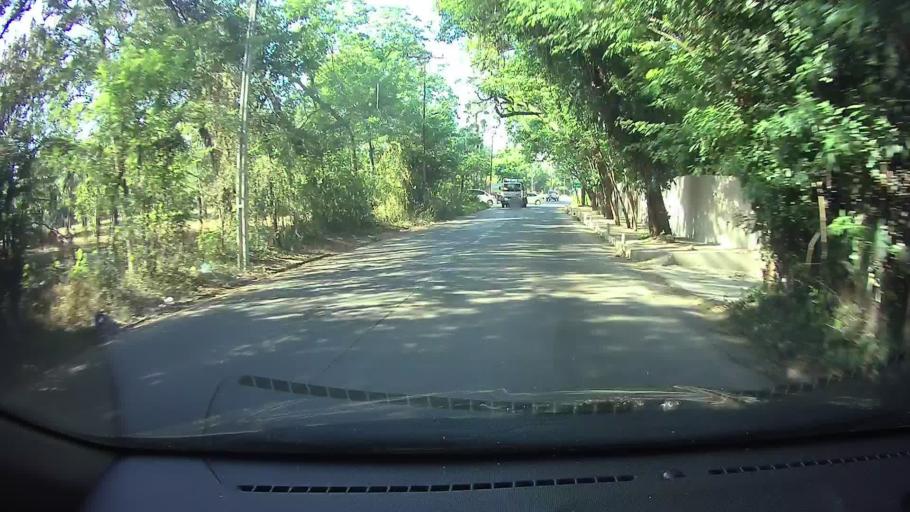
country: PY
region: Central
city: Fernando de la Mora
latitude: -25.2701
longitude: -57.5174
